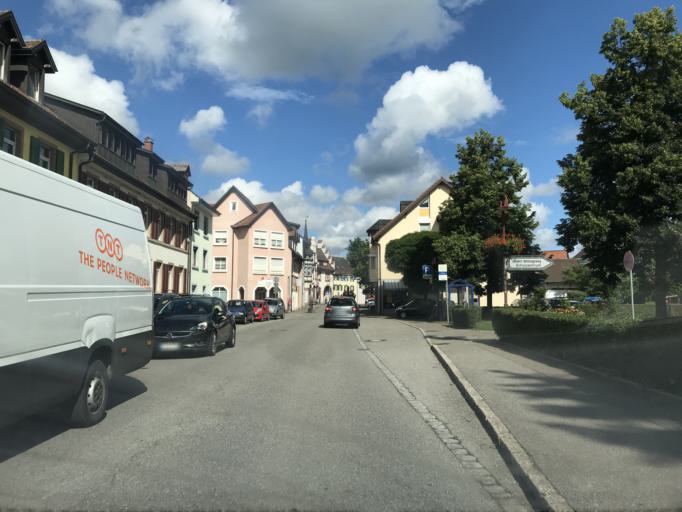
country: DE
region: Baden-Wuerttemberg
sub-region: Freiburg Region
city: Steinen
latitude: 47.6423
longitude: 7.7415
